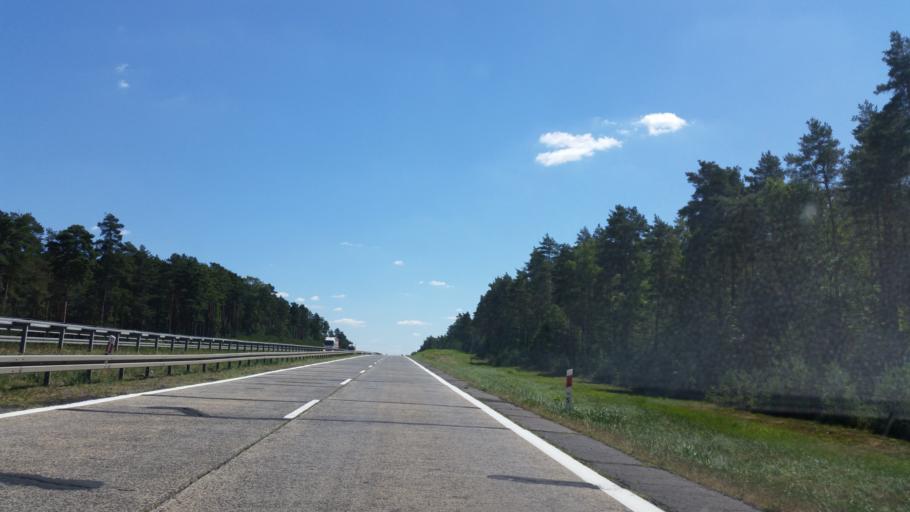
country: PL
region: Lower Silesian Voivodeship
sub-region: Powiat boleslawiecki
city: Boleslawiec
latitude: 51.4075
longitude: 15.5051
